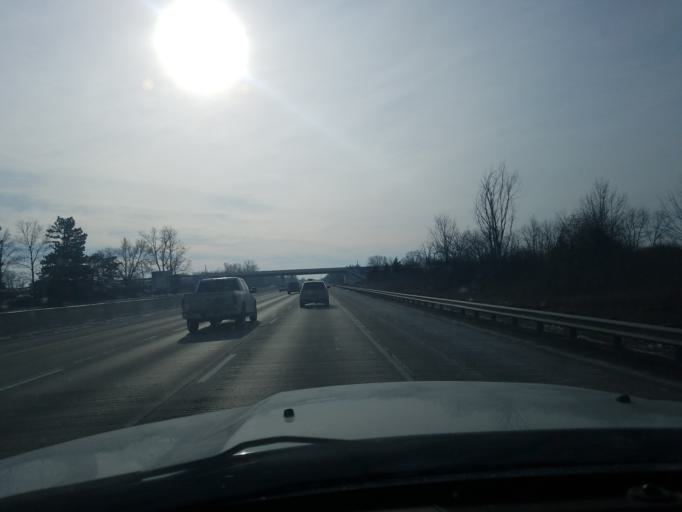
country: US
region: Indiana
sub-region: Allen County
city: Fort Wayne
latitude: 41.1046
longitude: -85.2051
